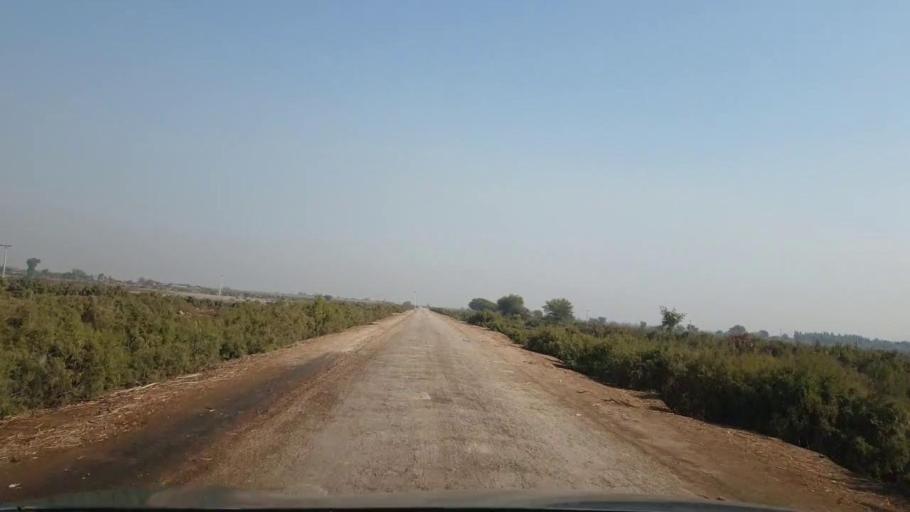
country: PK
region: Sindh
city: Berani
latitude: 25.6402
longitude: 68.8702
